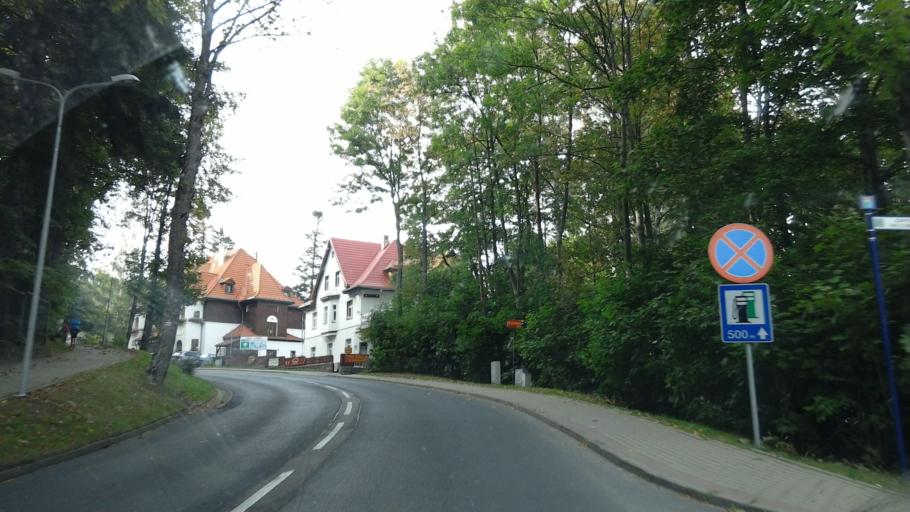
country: PL
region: Lower Silesian Voivodeship
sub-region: Powiat jeleniogorski
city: Karpacz
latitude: 50.7757
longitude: 15.7448
